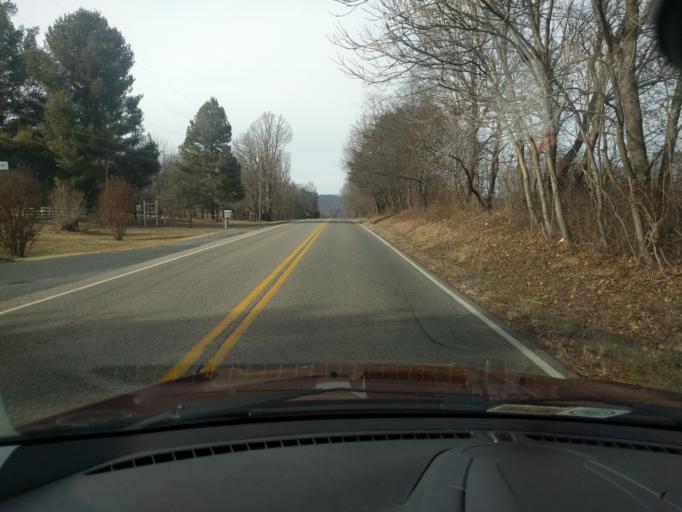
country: US
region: Virginia
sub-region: Augusta County
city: Stuarts Draft
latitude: 38.0369
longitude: -79.0738
